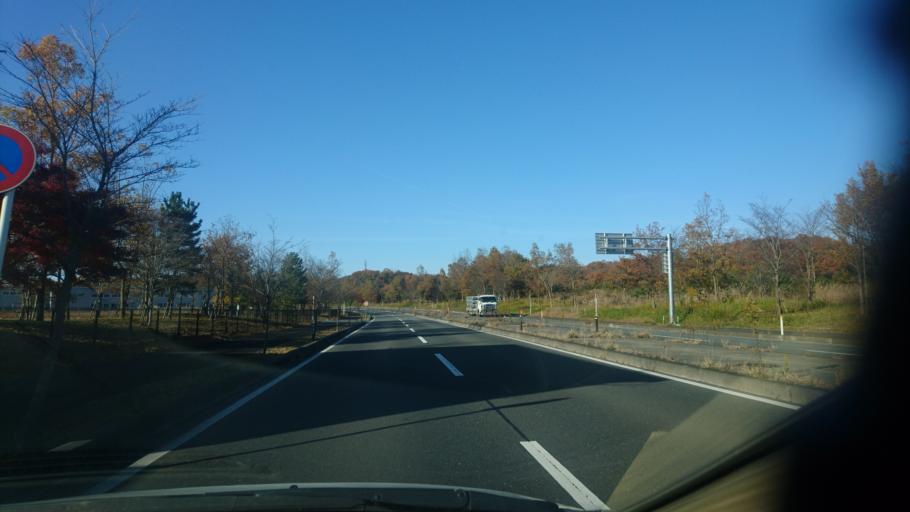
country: JP
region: Miyagi
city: Tomiya
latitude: 38.4702
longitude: 140.9069
